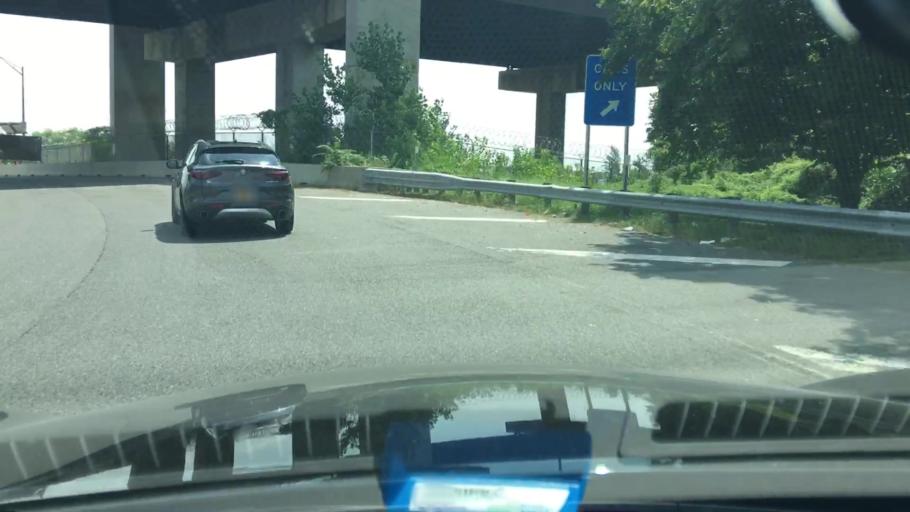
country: US
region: New Jersey
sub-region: Bergen County
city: Moonachie
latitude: 40.8251
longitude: -74.0327
